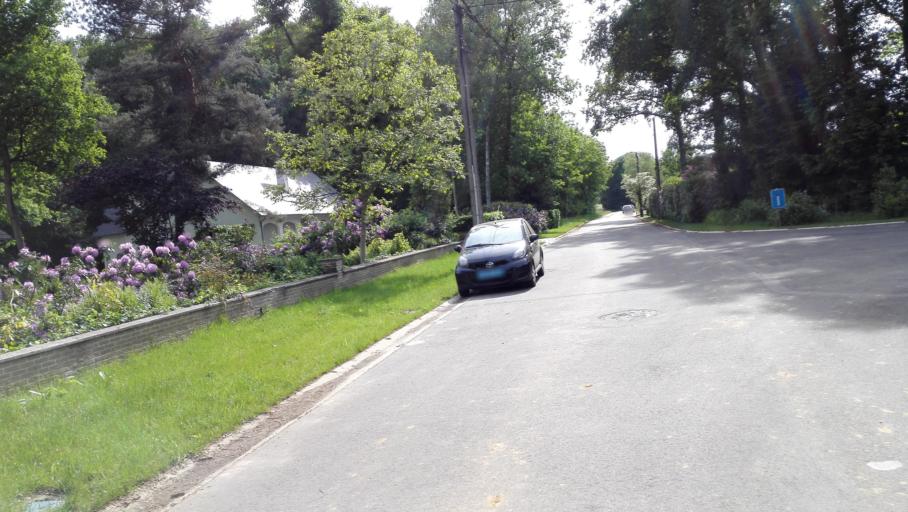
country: BE
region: Flanders
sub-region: Provincie Vlaams-Brabant
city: Holsbeek
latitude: 50.9039
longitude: 4.7760
